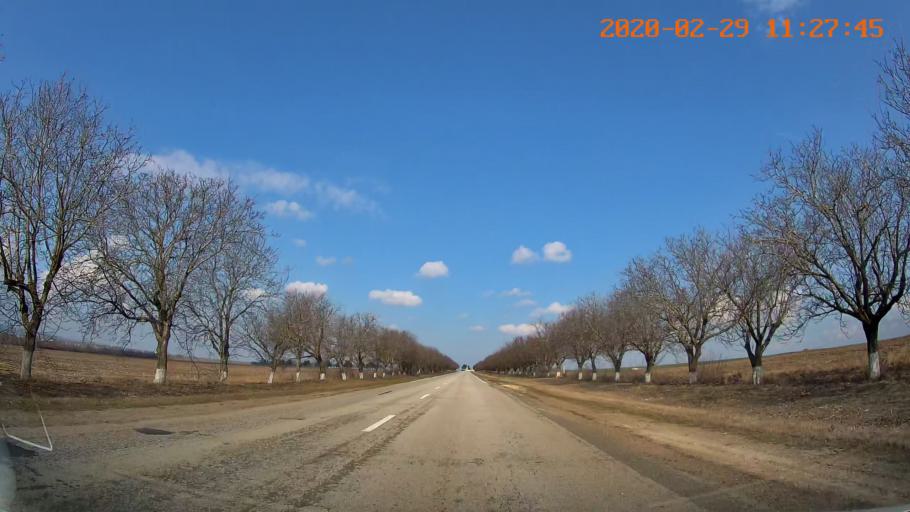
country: MD
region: Telenesti
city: Cocieri
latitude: 47.4731
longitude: 29.1412
